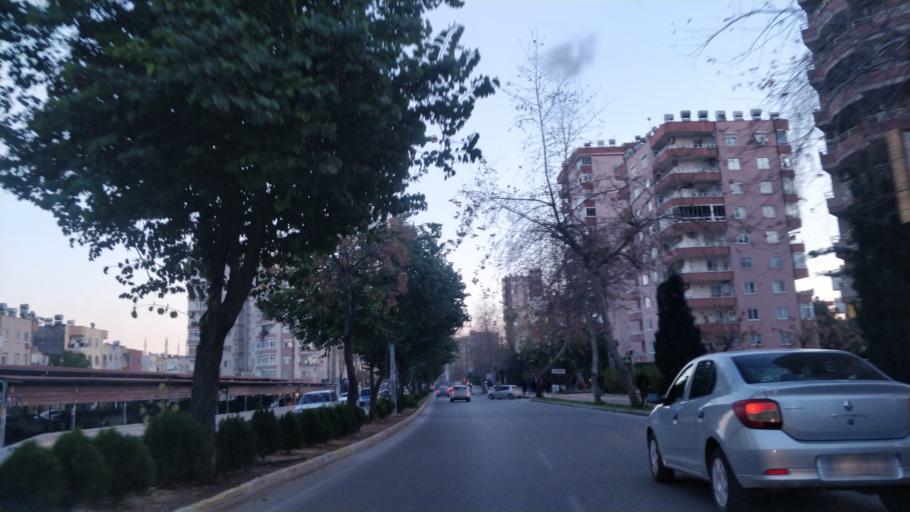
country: TR
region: Mersin
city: Mercin
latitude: 36.7891
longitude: 34.5927
